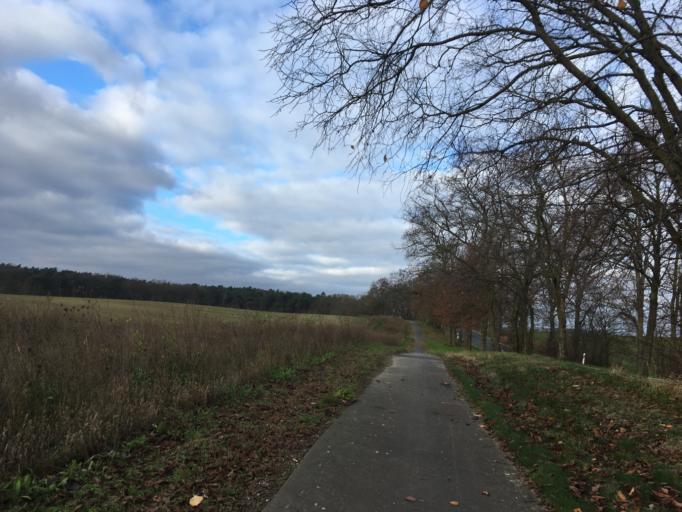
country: DE
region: Brandenburg
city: Muncheberg
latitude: 52.5493
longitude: 14.1562
